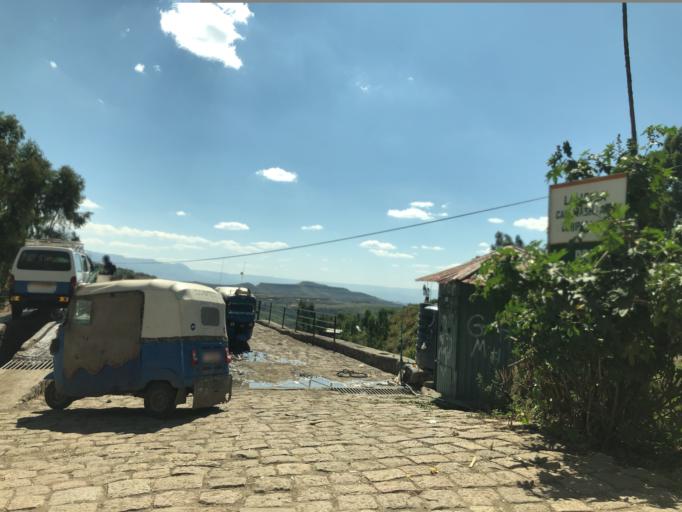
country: ET
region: Amhara
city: Lalibela
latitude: 12.0311
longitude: 39.0486
